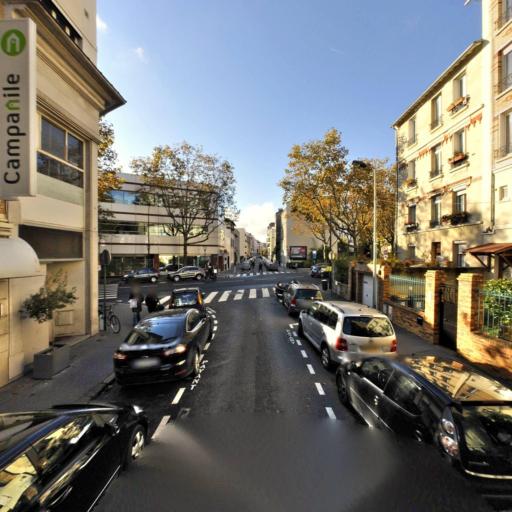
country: FR
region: Ile-de-France
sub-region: Departement des Hauts-de-Seine
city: Boulogne-Billancourt
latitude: 48.8347
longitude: 2.2424
